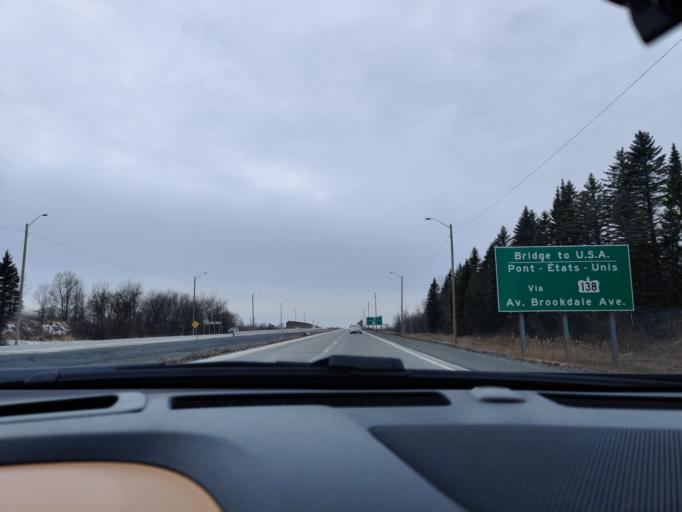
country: CA
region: Ontario
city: Cornwall
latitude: 45.0522
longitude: -74.7493
